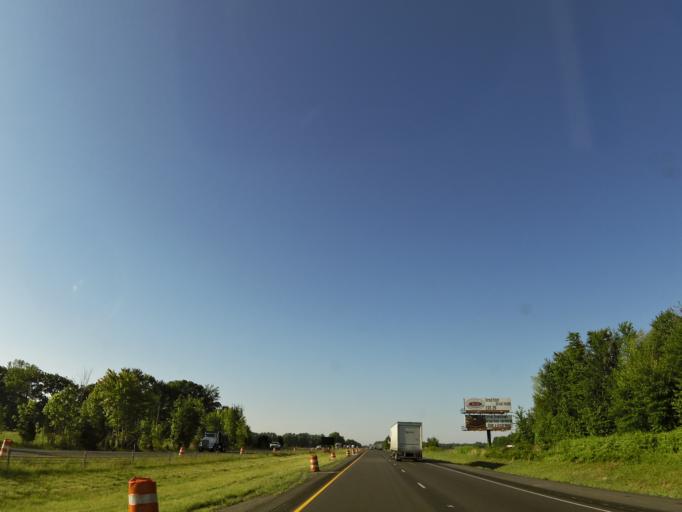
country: US
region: Indiana
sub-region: Jackson County
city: Crothersville
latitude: 38.8835
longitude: -85.8105
